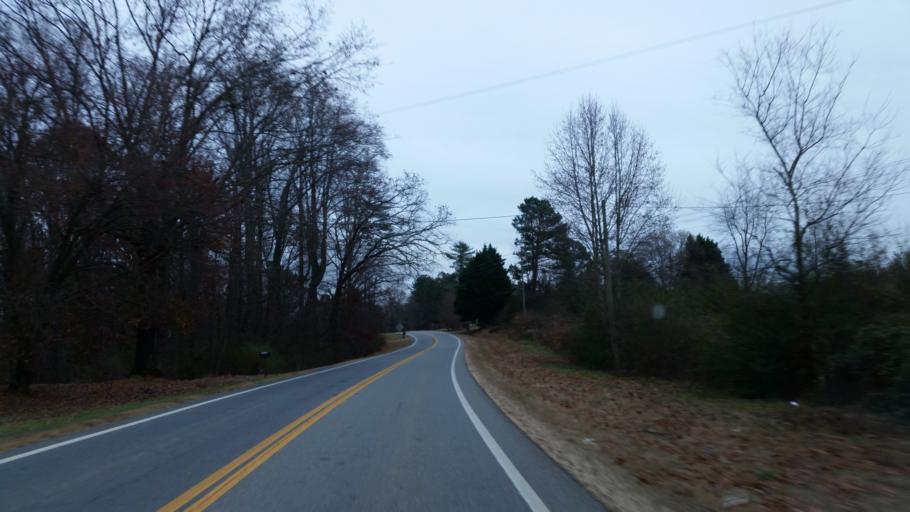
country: US
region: Georgia
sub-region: Dawson County
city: Dawsonville
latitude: 34.4861
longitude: -84.1694
